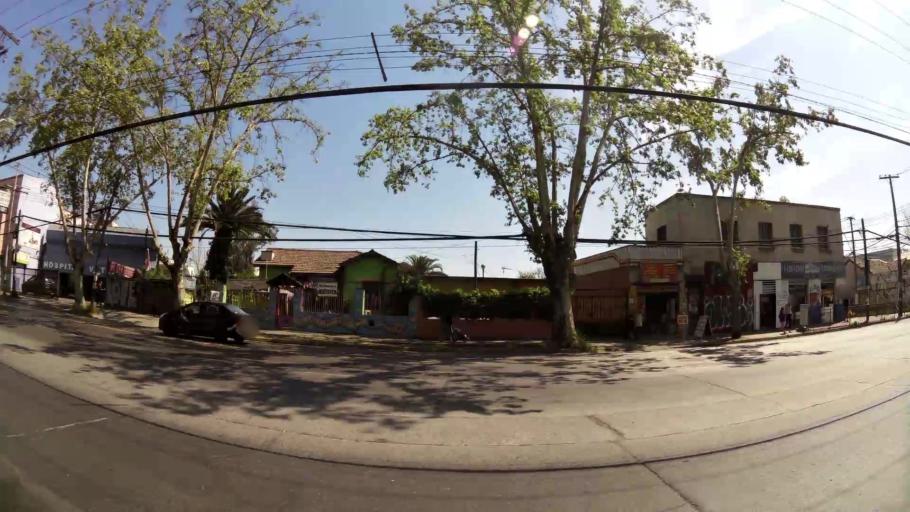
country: CL
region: Santiago Metropolitan
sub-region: Provincia de Santiago
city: La Pintana
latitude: -33.5475
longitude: -70.6698
